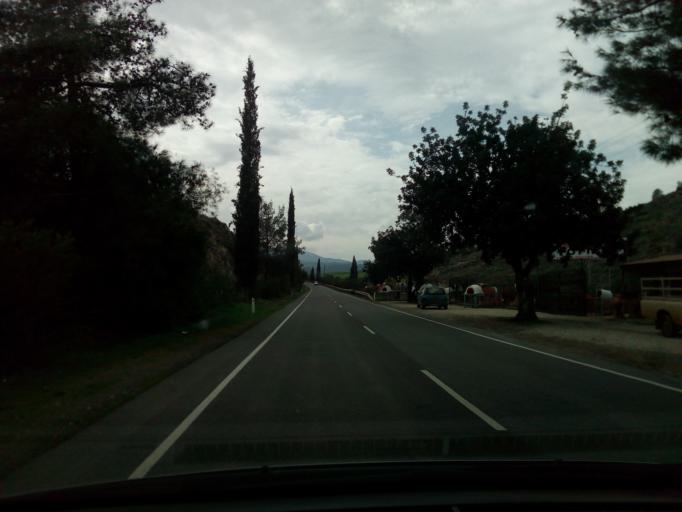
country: CY
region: Lefkosia
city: Astromeritis
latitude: 35.0953
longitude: 32.9670
